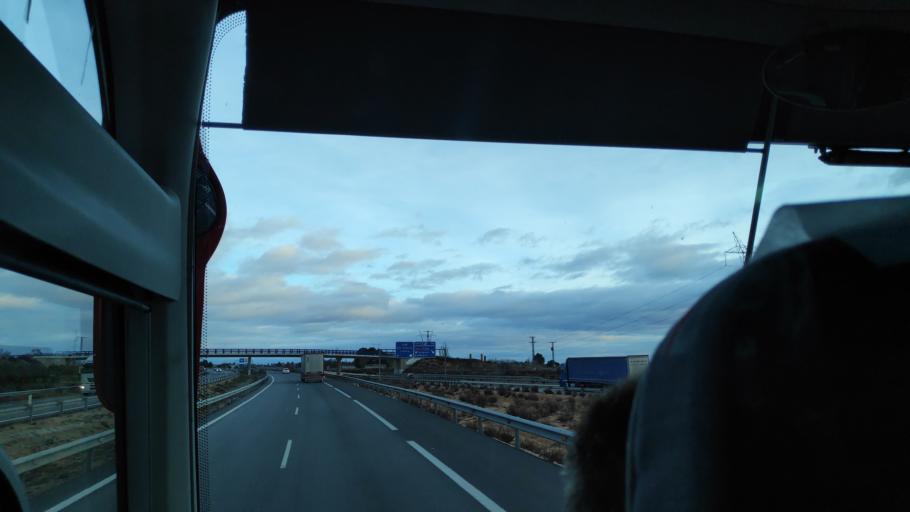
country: ES
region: Castille-La Mancha
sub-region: Provincia de Cuenca
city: Tarancon
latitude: 39.9984
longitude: -3.0198
